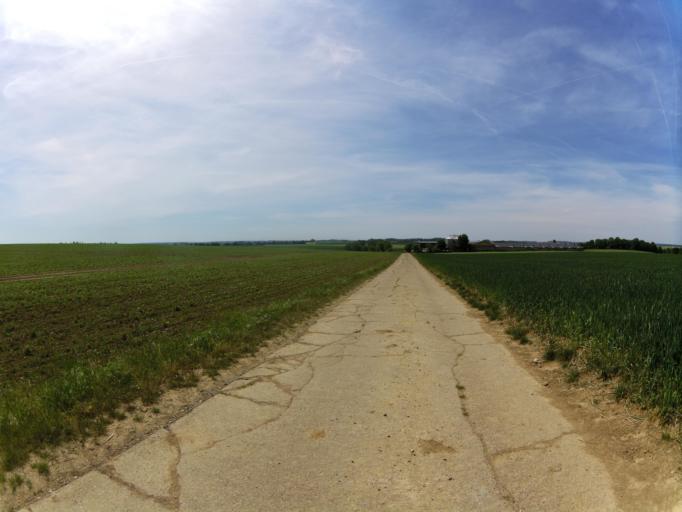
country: DE
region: Bavaria
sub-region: Regierungsbezirk Unterfranken
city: Sommerhausen
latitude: 49.6691
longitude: 10.0247
